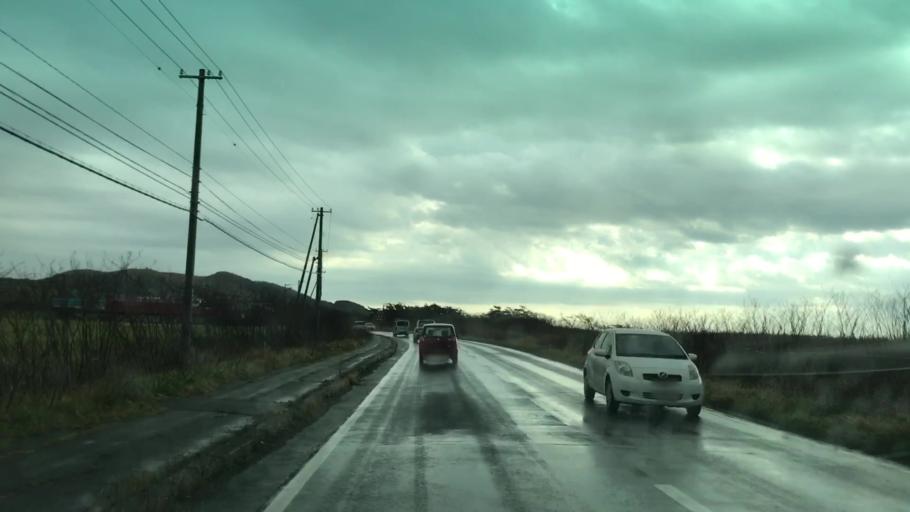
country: JP
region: Hokkaido
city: Shizunai-furukawacho
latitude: 42.1938
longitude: 142.6858
